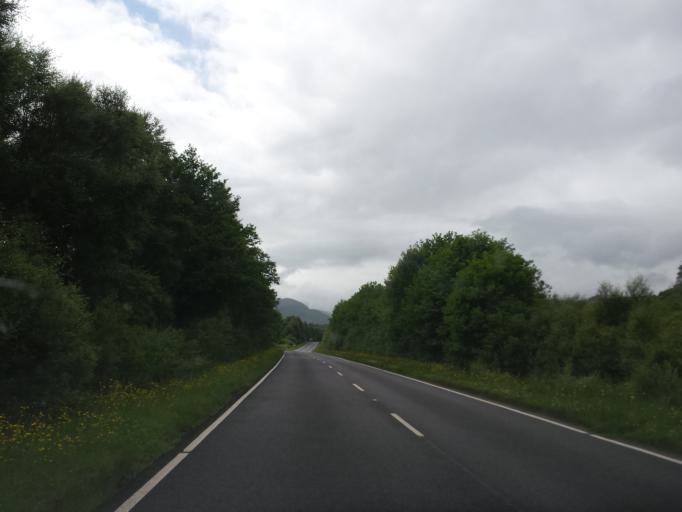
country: GB
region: Scotland
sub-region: Highland
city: Fort William
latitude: 56.8605
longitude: -5.3354
